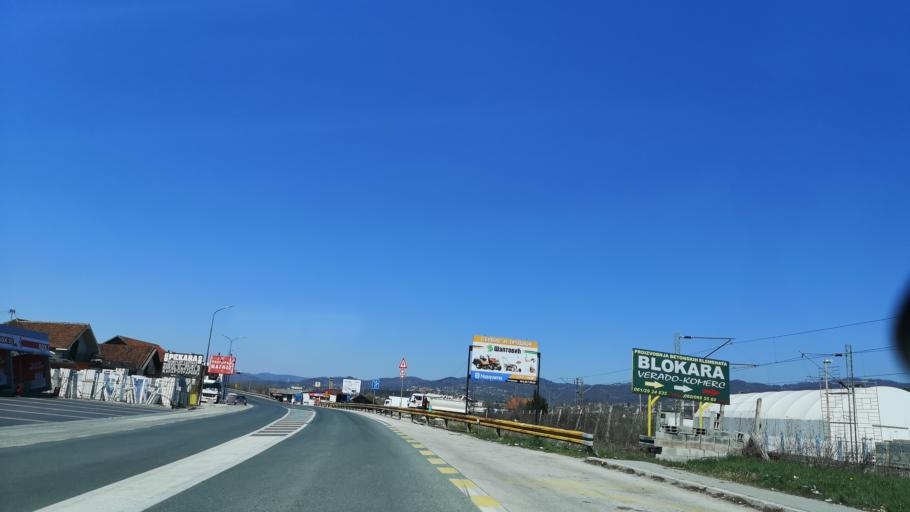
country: RS
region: Central Serbia
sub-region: Zlatiborski Okrug
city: Pozega
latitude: 43.8307
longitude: 20.0423
